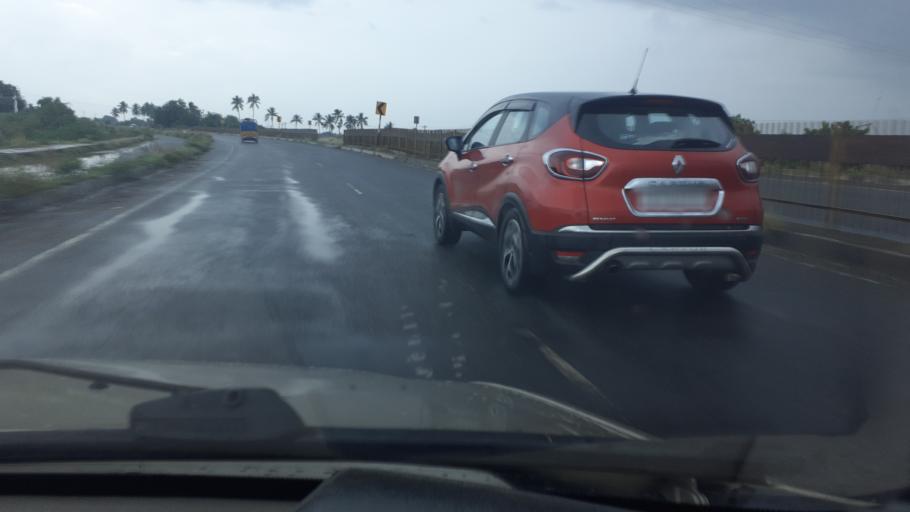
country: IN
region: Tamil Nadu
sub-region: Thoothukkudi
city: Kadambur
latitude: 9.0346
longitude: 77.7895
